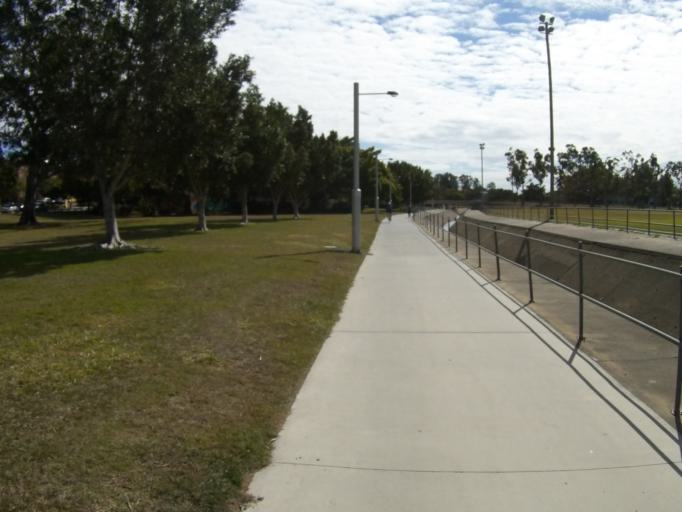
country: AU
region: Queensland
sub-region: Brisbane
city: Greenslopes
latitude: -27.5066
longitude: 153.0418
